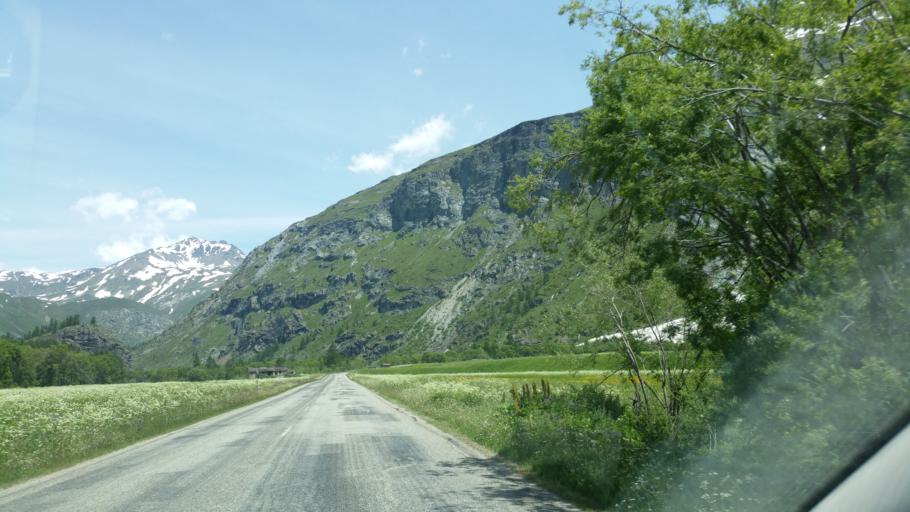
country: FR
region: Rhone-Alpes
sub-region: Departement de la Savoie
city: Val-d'Isere
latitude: 45.3363
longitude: 7.0214
